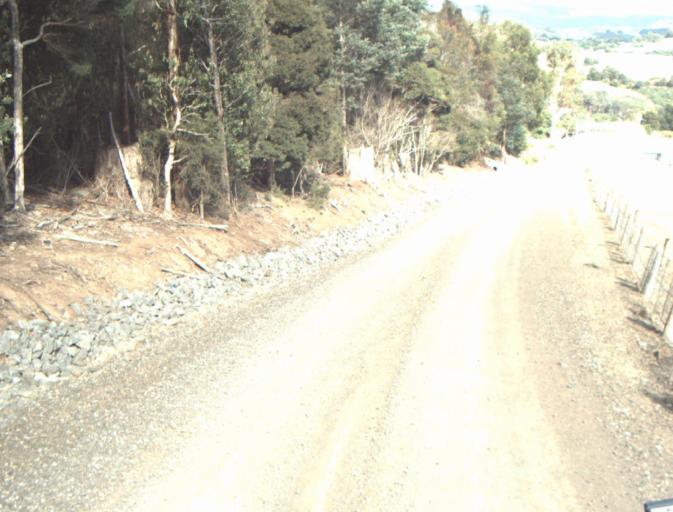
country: AU
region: Tasmania
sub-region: Launceston
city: Mayfield
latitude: -41.2627
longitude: 147.2216
